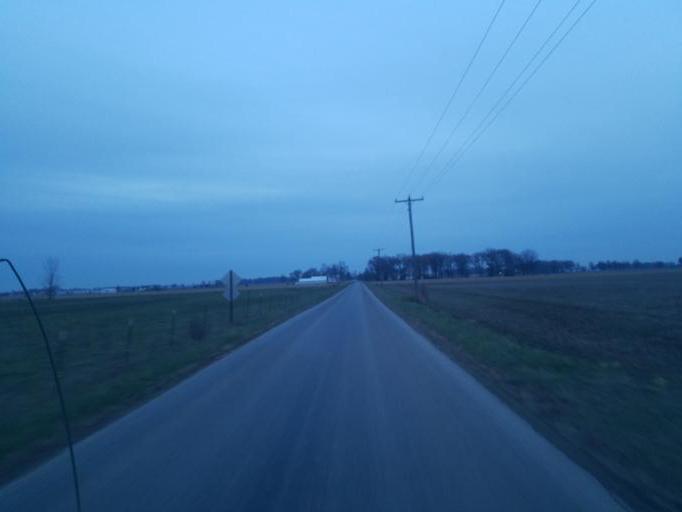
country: US
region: Indiana
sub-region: Adams County
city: Berne
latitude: 40.7304
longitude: -84.9725
